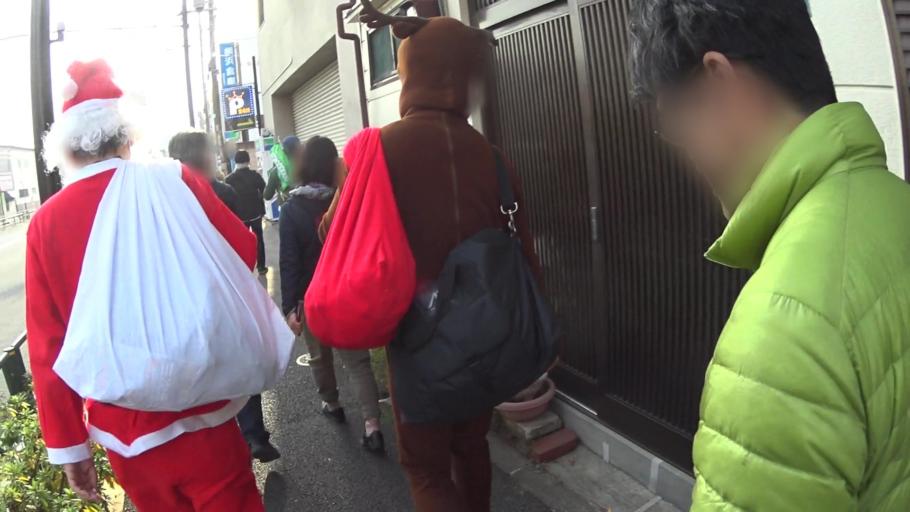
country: JP
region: Tokyo
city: Urayasu
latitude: 35.7224
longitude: 139.8120
